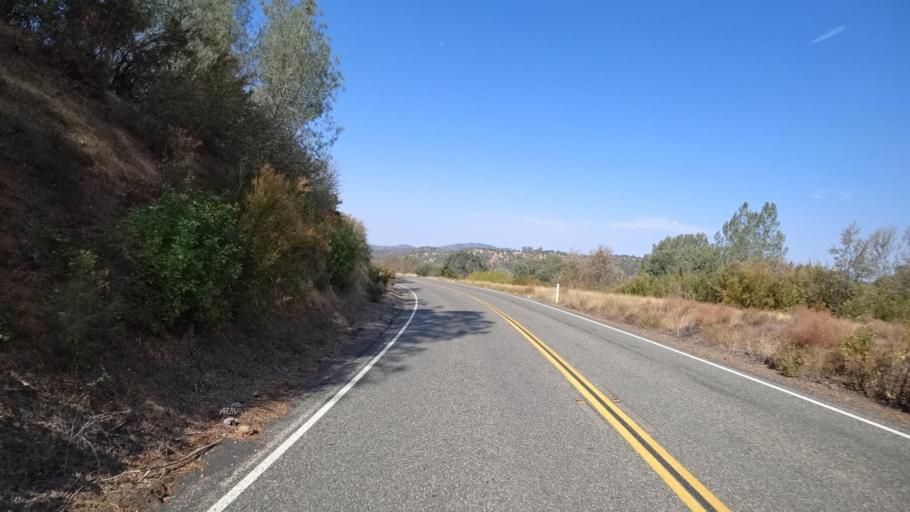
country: US
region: California
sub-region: Tuolumne County
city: Tuolumne City
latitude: 37.7396
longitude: -120.1761
